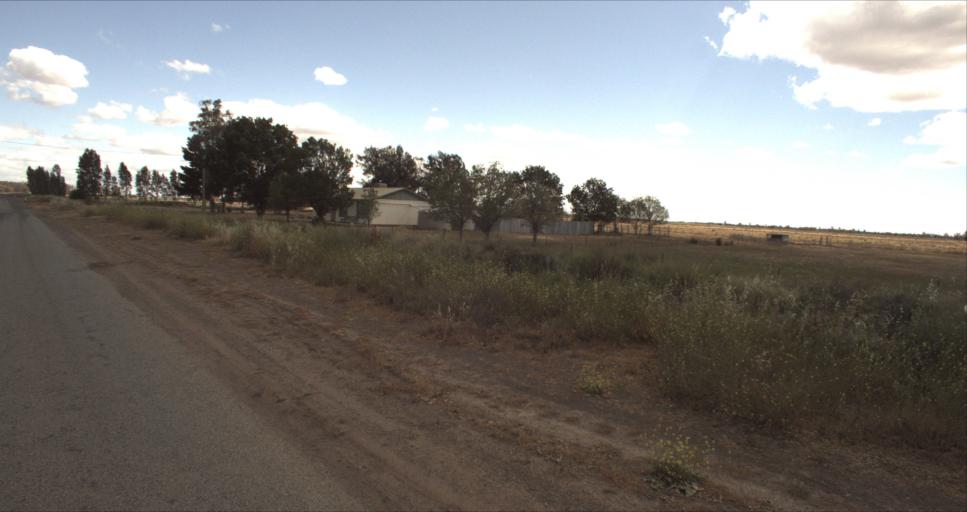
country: AU
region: New South Wales
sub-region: Leeton
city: Leeton
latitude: -34.5249
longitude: 146.2217
